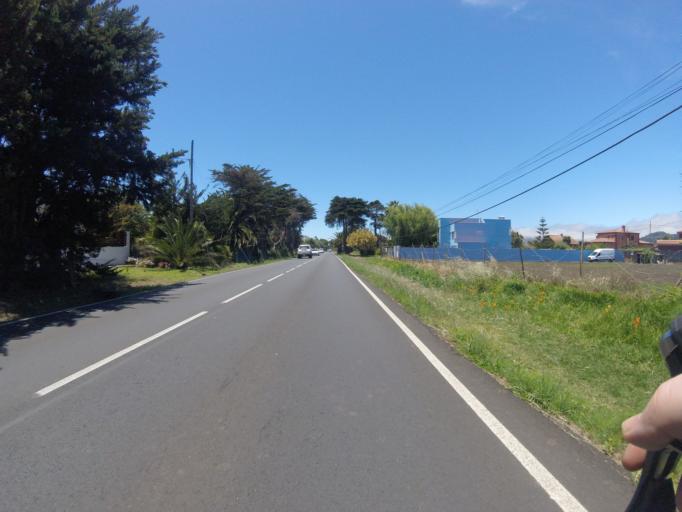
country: ES
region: Canary Islands
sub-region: Provincia de Santa Cruz de Tenerife
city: Tegueste
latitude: 28.5024
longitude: -16.3127
